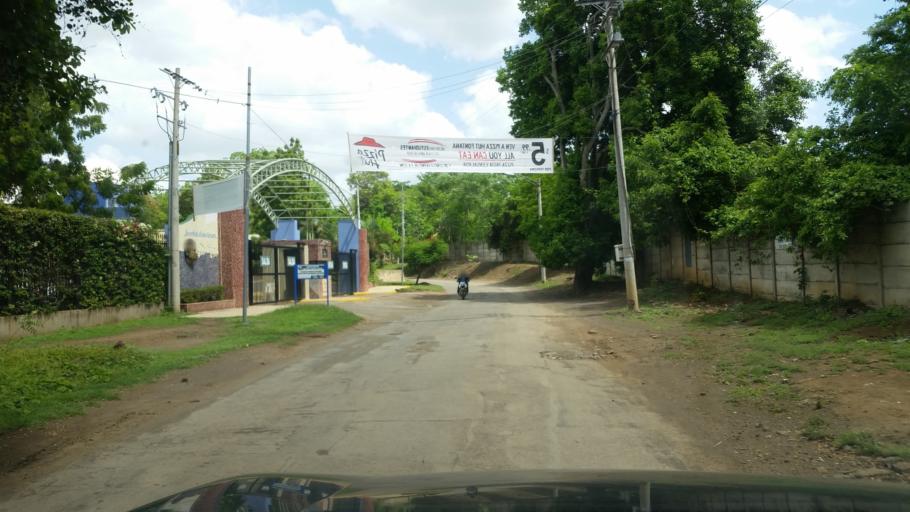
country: NI
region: Managua
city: Managua
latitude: 12.0915
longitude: -86.2231
